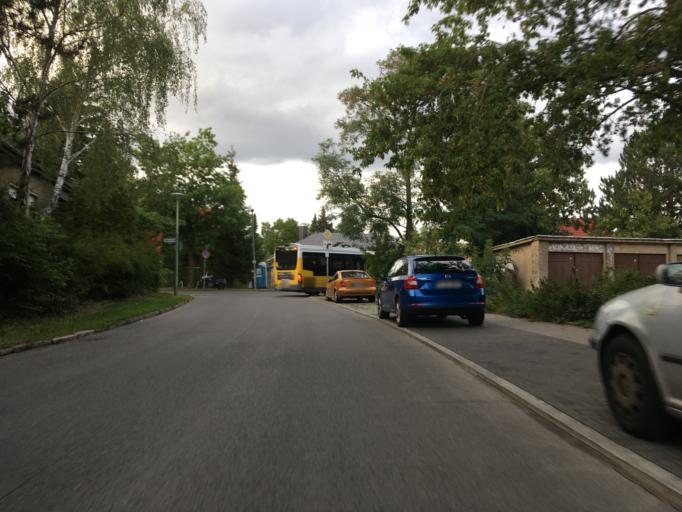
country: DE
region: Berlin
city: Johannisthal
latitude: 52.4413
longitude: 13.4950
